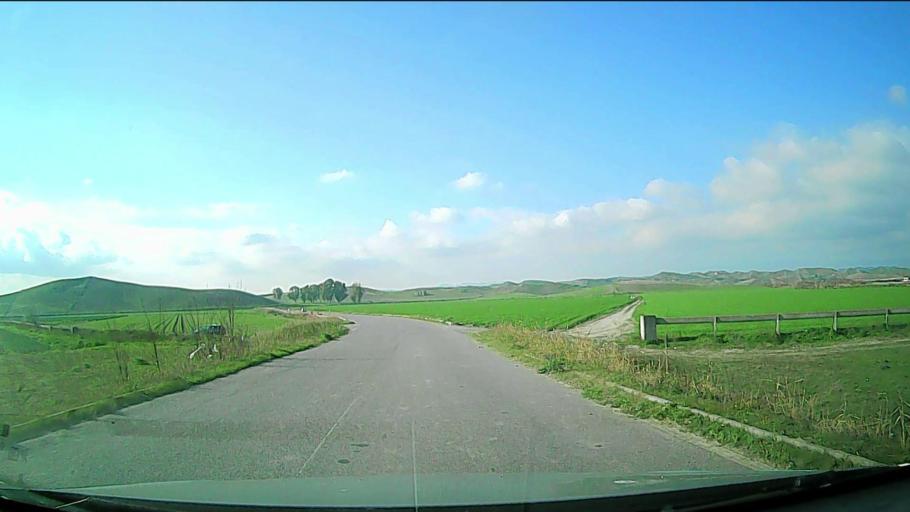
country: IT
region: Calabria
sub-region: Provincia di Crotone
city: Tronca
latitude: 39.2005
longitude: 17.0667
